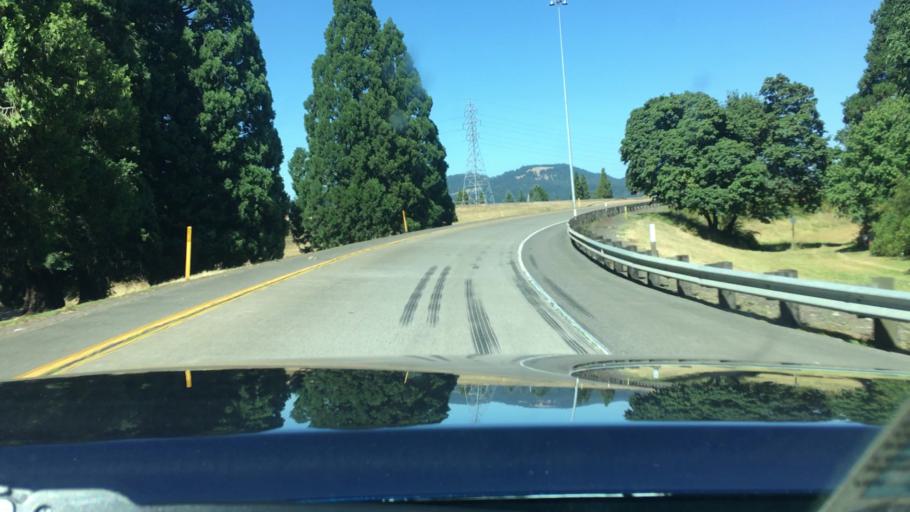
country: US
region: Oregon
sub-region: Lane County
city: Springfield
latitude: 44.0613
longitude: -123.0488
